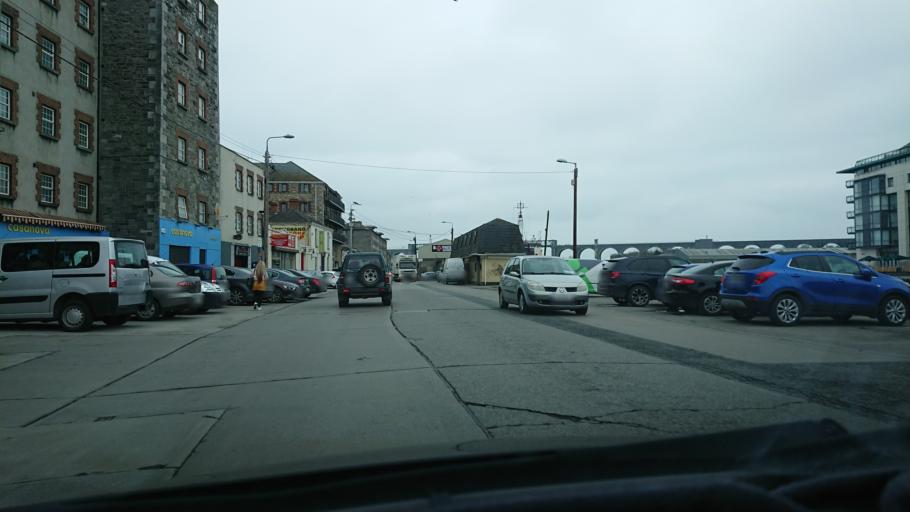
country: IE
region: Leinster
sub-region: Lu
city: Drogheda
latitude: 53.7147
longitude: -6.3469
